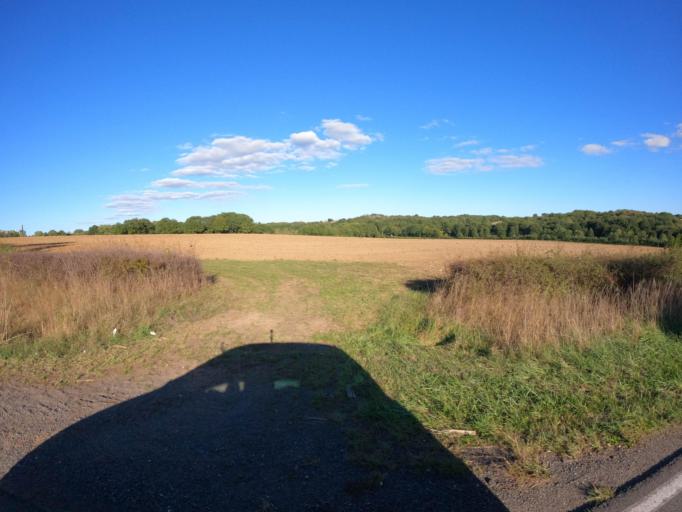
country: FR
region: Bourgogne
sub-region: Departement de Saone-et-Loire
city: Torcy
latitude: 46.7517
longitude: 4.4408
